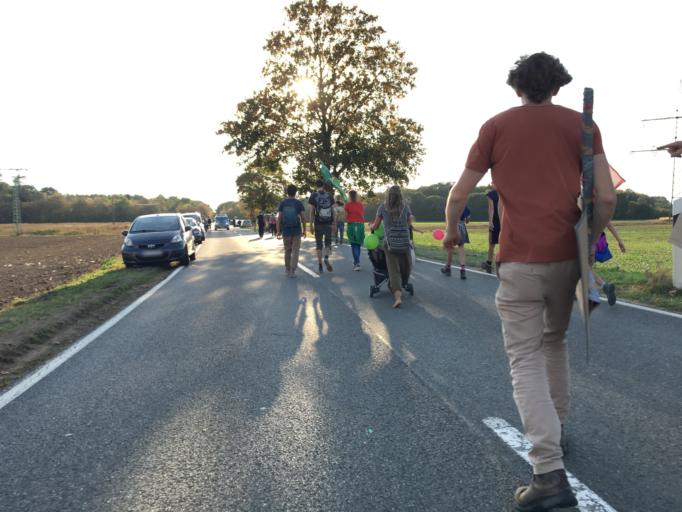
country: DE
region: North Rhine-Westphalia
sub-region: Regierungsbezirk Koln
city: Merzenich
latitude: 50.8630
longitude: 6.5324
